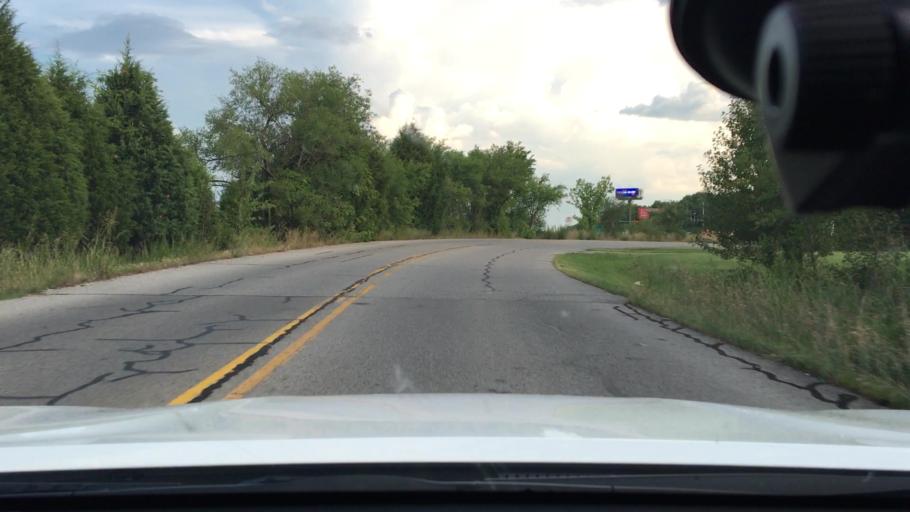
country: US
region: Arkansas
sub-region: Benton County
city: Bentonville
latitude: 36.3371
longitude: -94.1840
